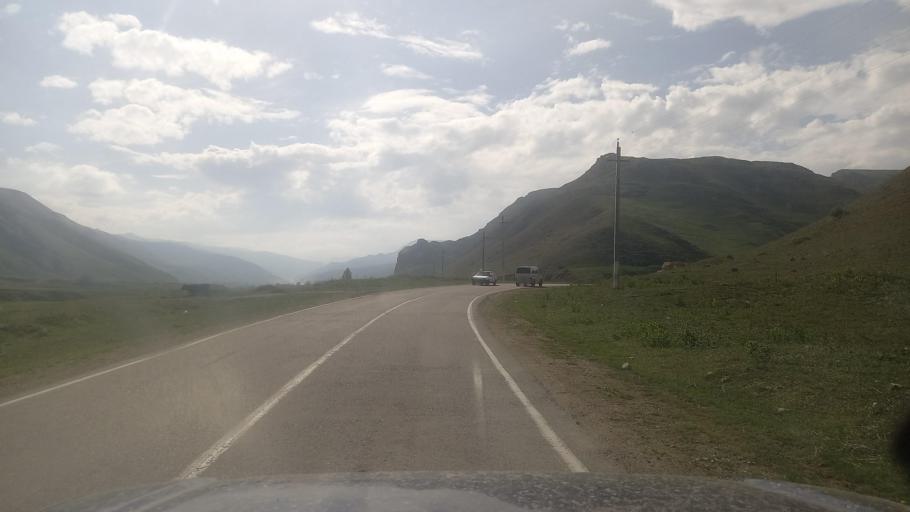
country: RU
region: Kabardino-Balkariya
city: Kamennomostskoye
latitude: 43.7343
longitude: 42.9742
